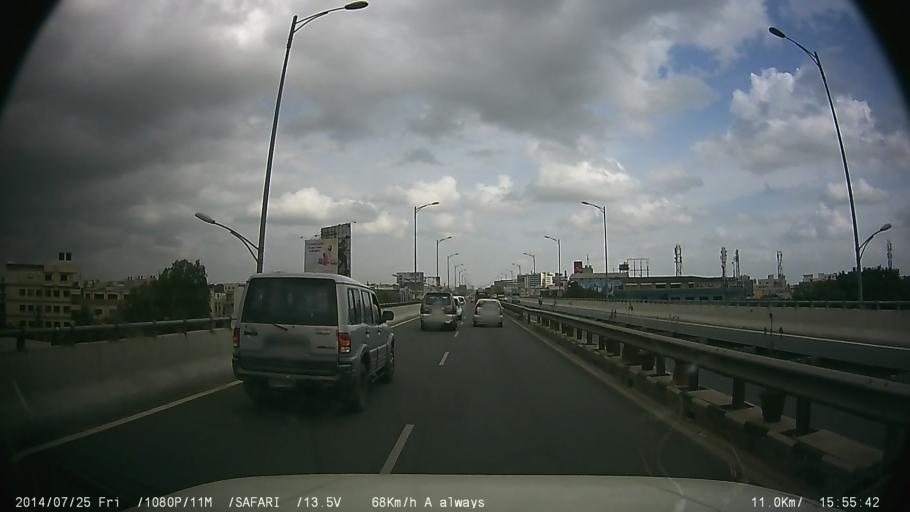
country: IN
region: Karnataka
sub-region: Bangalore Urban
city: Bangalore
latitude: 12.9006
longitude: 77.6330
